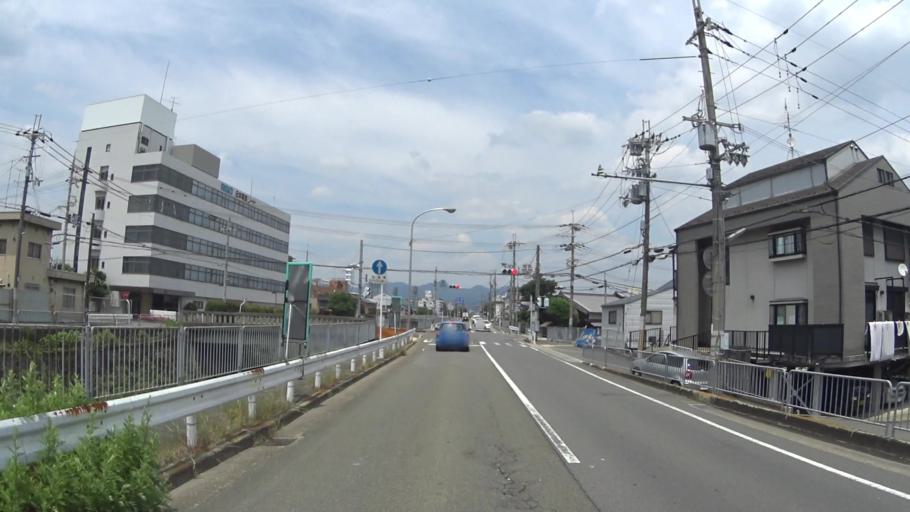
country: JP
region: Kyoto
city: Muko
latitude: 34.9869
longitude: 135.7182
